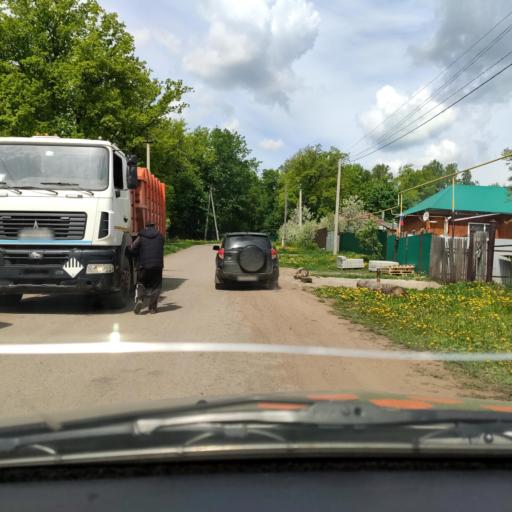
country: RU
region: Bashkortostan
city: Avdon
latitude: 54.6488
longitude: 55.7032
